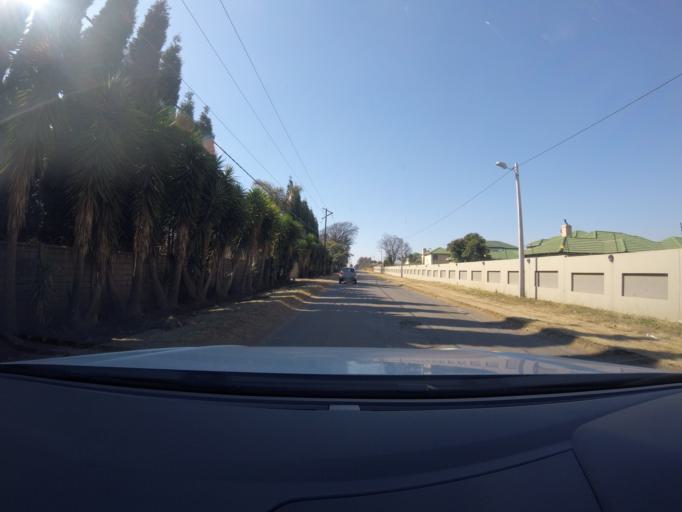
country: ZA
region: Gauteng
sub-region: Ekurhuleni Metropolitan Municipality
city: Benoni
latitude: -26.1236
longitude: 28.2881
